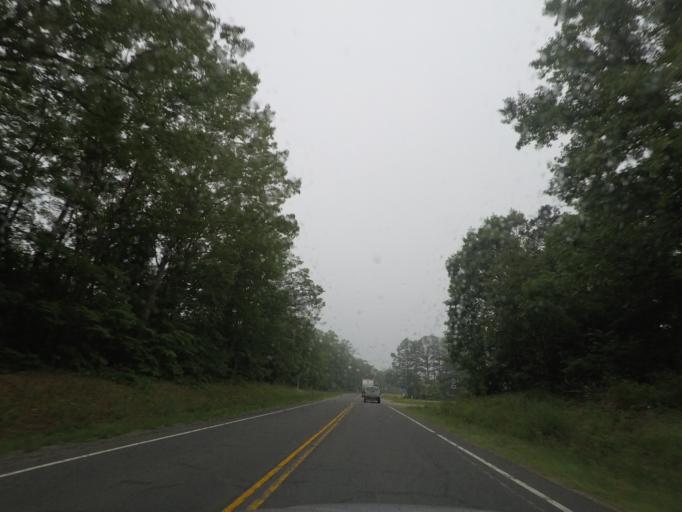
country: US
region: Virginia
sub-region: Buckingham County
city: Buckingham
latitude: 37.5064
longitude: -78.4813
